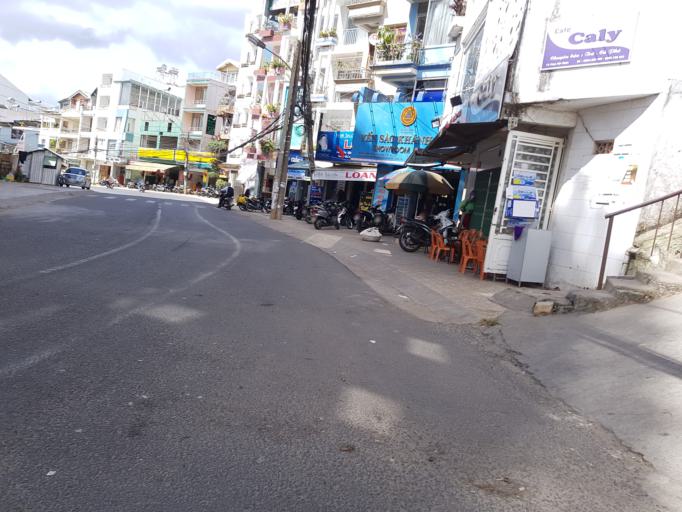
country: VN
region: Lam Dong
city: Da Lat
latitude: 11.9444
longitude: 108.4383
